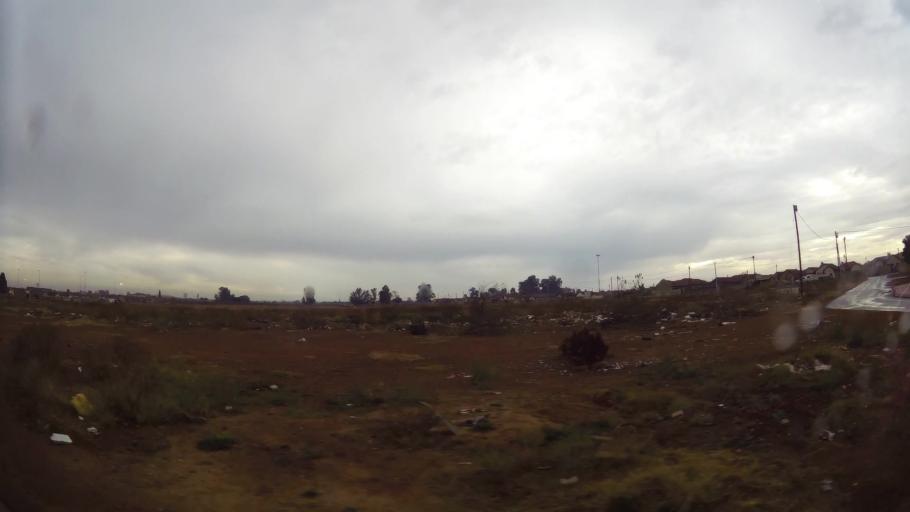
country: ZA
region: Gauteng
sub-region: Ekurhuleni Metropolitan Municipality
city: Germiston
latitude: -26.3318
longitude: 28.1989
